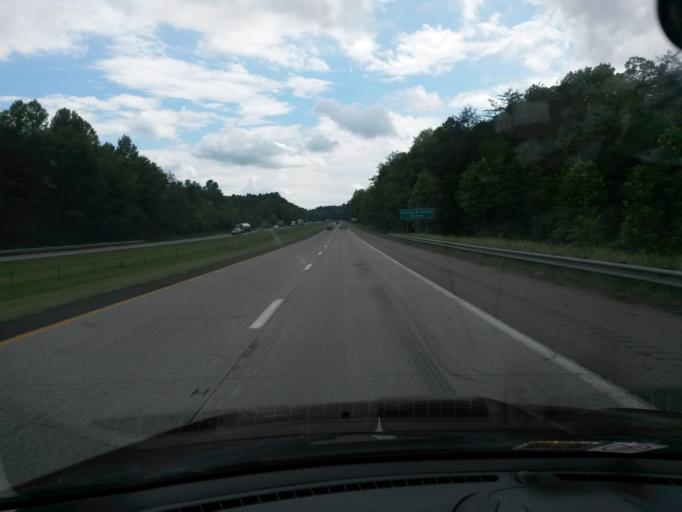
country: US
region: Virginia
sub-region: Carroll County
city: Cana
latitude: 36.5456
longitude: -80.7466
